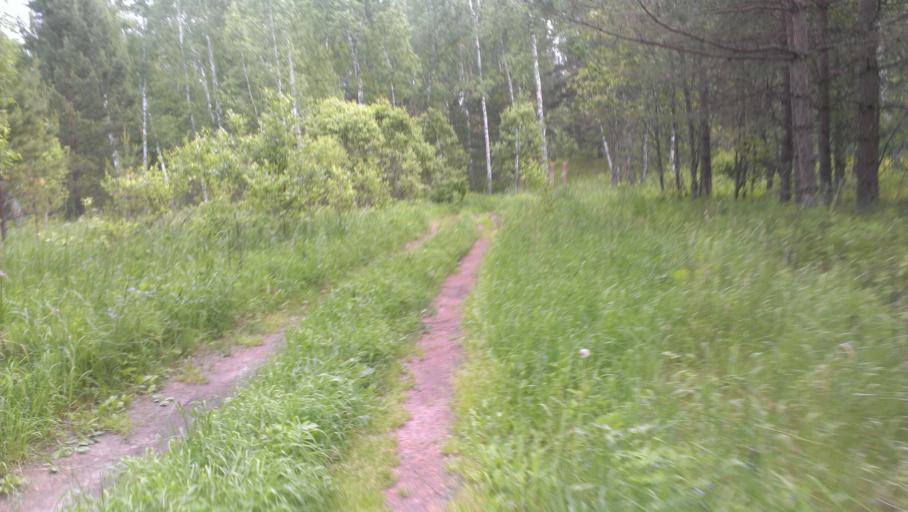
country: RU
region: Altai Krai
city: Sannikovo
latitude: 53.3484
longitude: 84.0388
